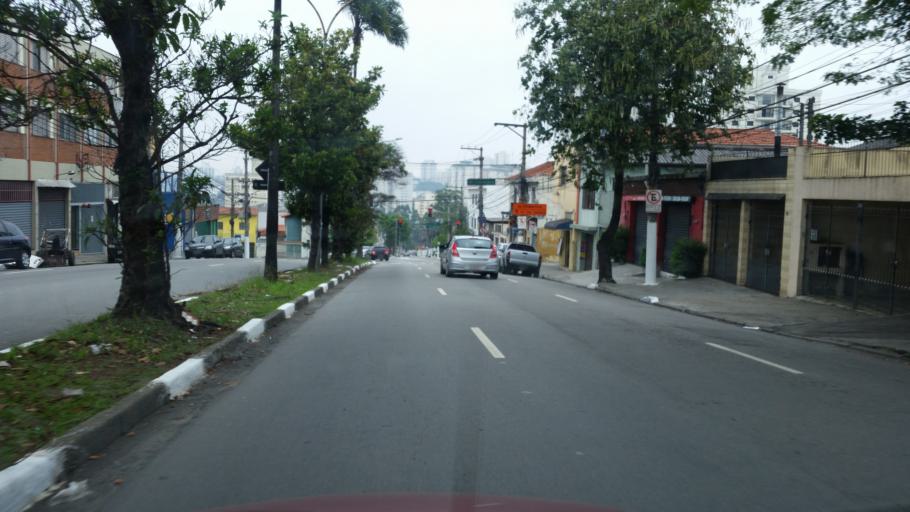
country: BR
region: Sao Paulo
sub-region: Diadema
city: Diadema
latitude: -23.6339
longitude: -46.6604
